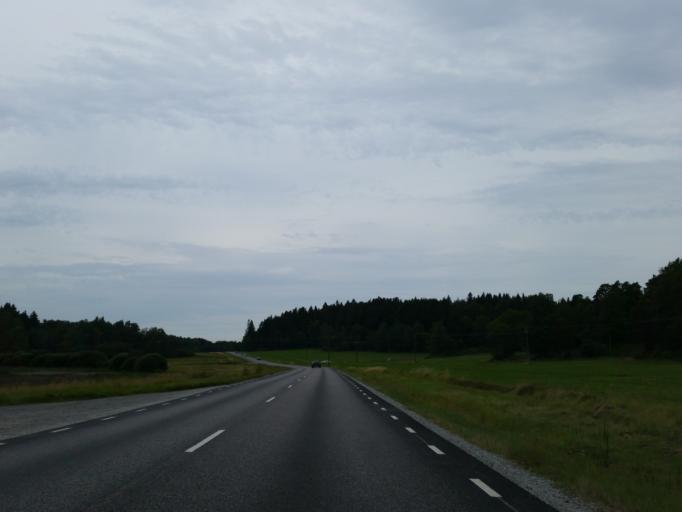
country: SE
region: Stockholm
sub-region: Salems Kommun
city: Ronninge
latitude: 59.2259
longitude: 17.7330
